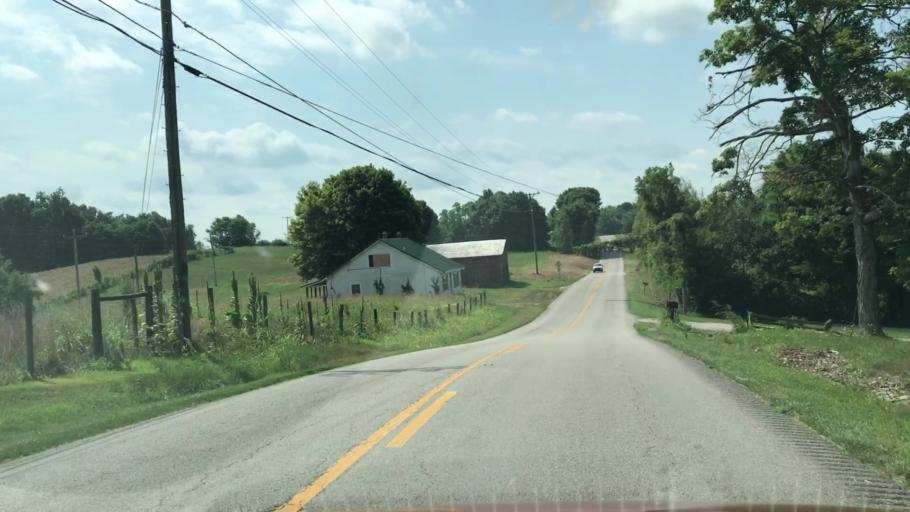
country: US
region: Kentucky
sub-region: Barren County
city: Glasgow
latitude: 36.8965
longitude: -85.8575
